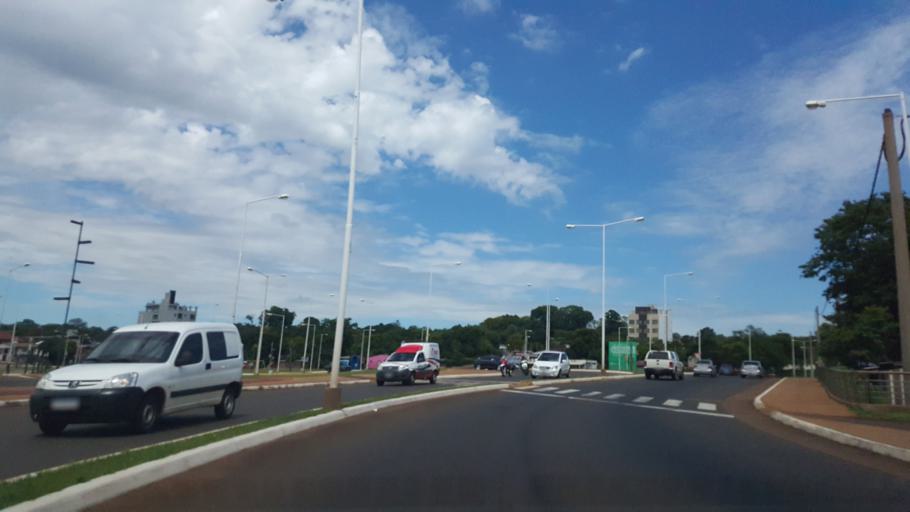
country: AR
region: Misiones
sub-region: Departamento de Capital
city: Posadas
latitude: -27.4029
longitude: -55.8926
